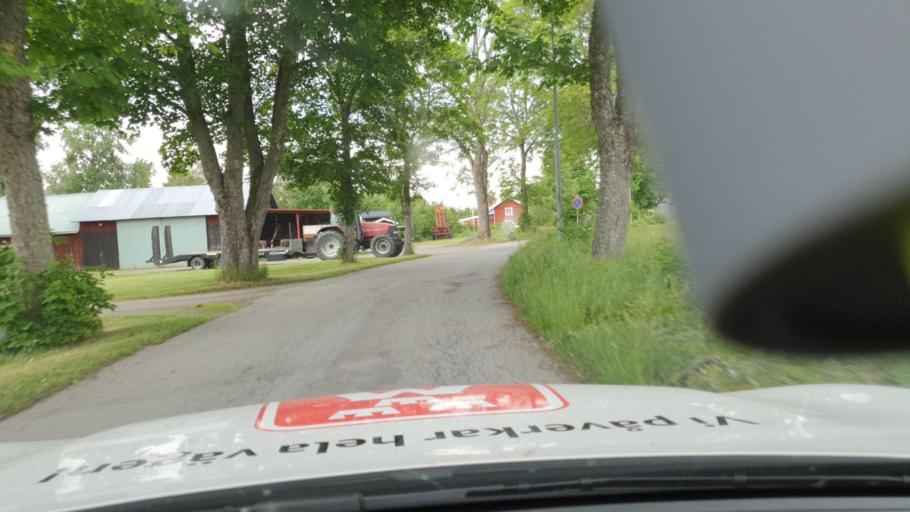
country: SE
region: OErebro
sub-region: Laxa Kommun
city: Laxa
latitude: 58.7706
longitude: 14.5312
